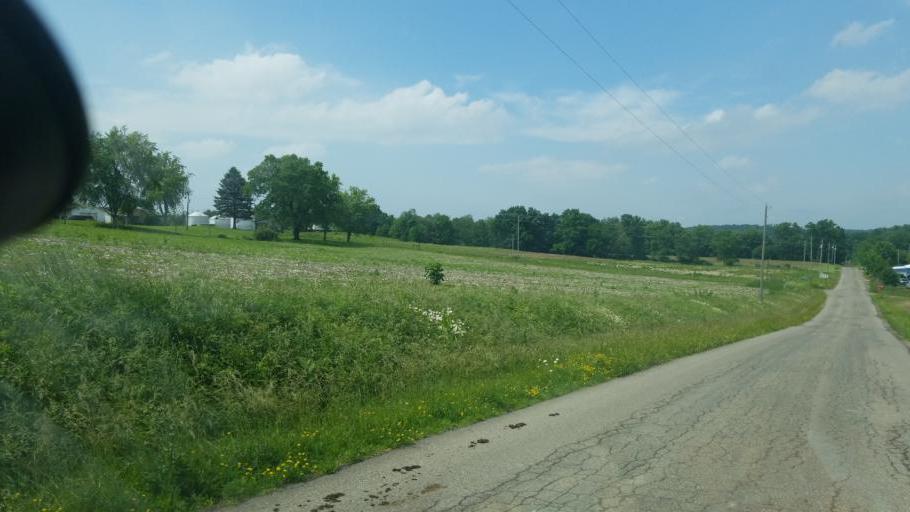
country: US
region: Ohio
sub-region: Knox County
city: Oak Hill
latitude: 40.3088
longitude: -82.2115
